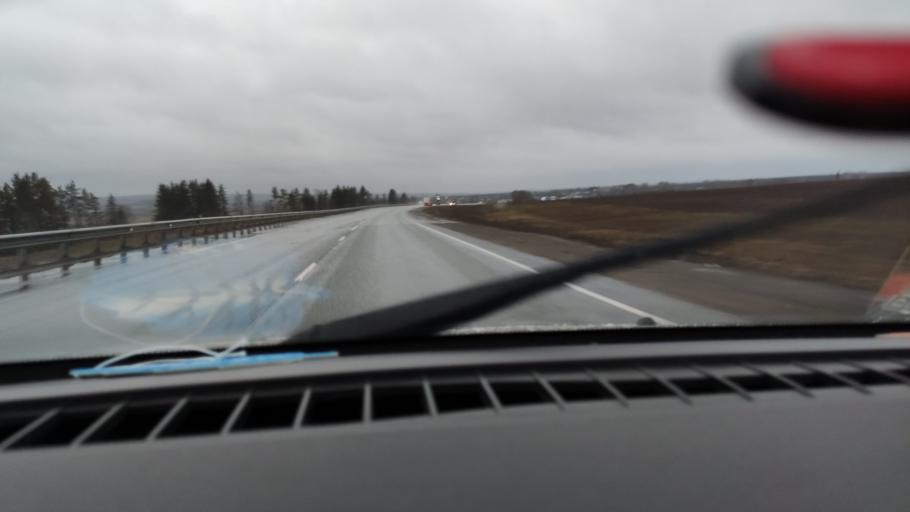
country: RU
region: Tatarstan
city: Mendeleyevsk
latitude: 56.0370
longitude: 52.3846
